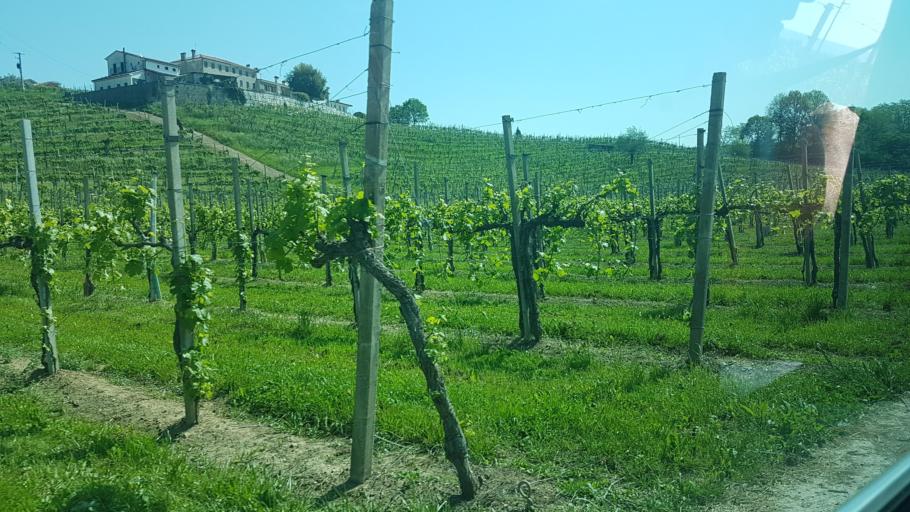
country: IT
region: Veneto
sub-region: Provincia di Treviso
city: Bigolino
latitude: 45.8785
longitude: 12.0121
